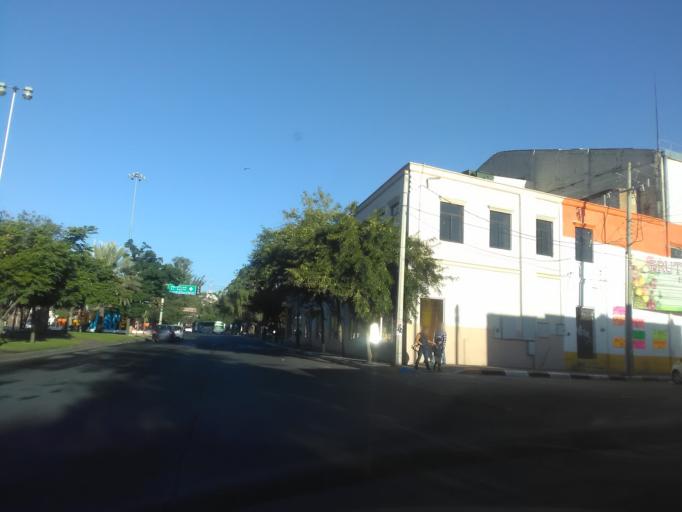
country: MX
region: Durango
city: Victoria de Durango
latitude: 24.0201
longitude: -104.6673
